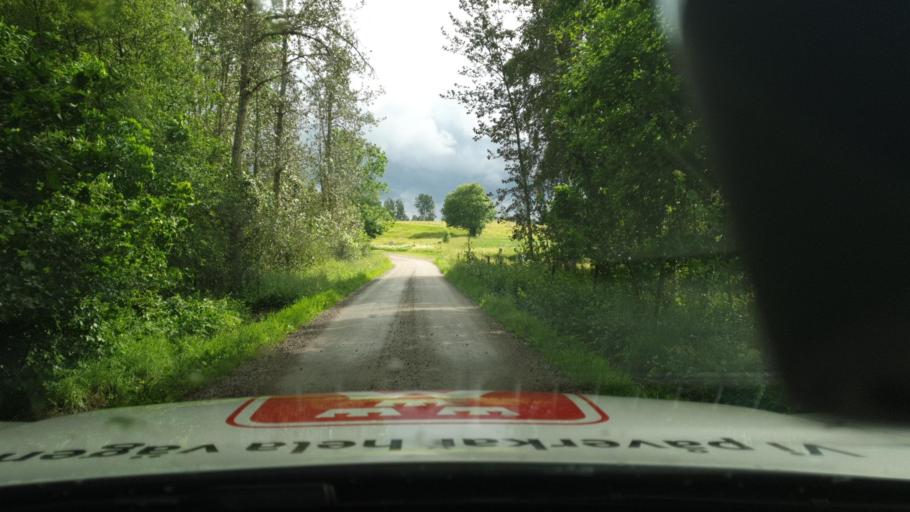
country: SE
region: Vaestra Goetaland
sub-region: Falkopings Kommun
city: Falkoeping
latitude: 58.0578
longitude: 13.6596
